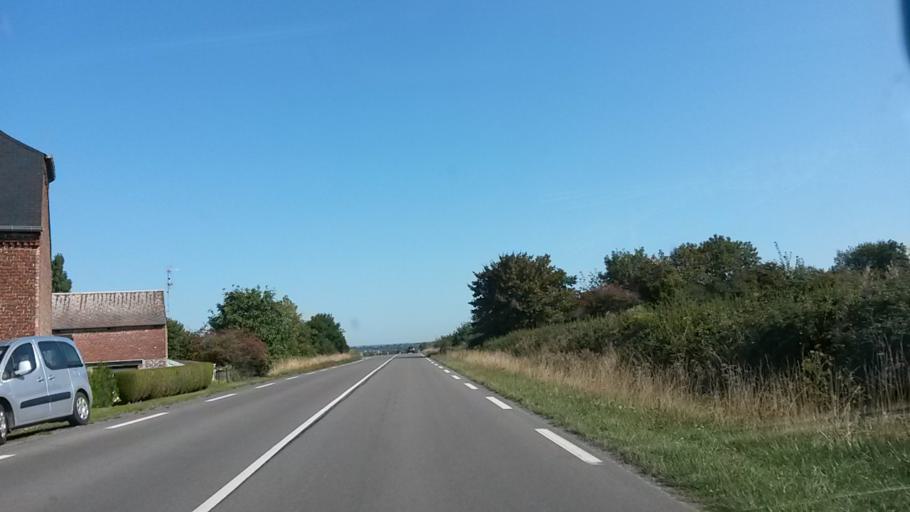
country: FR
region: Picardie
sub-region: Departement de l'Aisne
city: La Flamengrie
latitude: 50.0383
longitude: 3.9251
